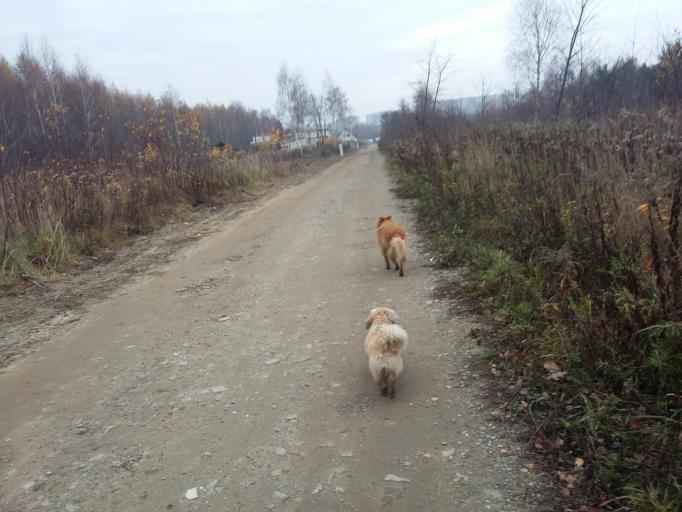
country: PL
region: Lodz Voivodeship
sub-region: Powiat pabianicki
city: Ksawerow
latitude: 51.7352
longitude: 19.4020
